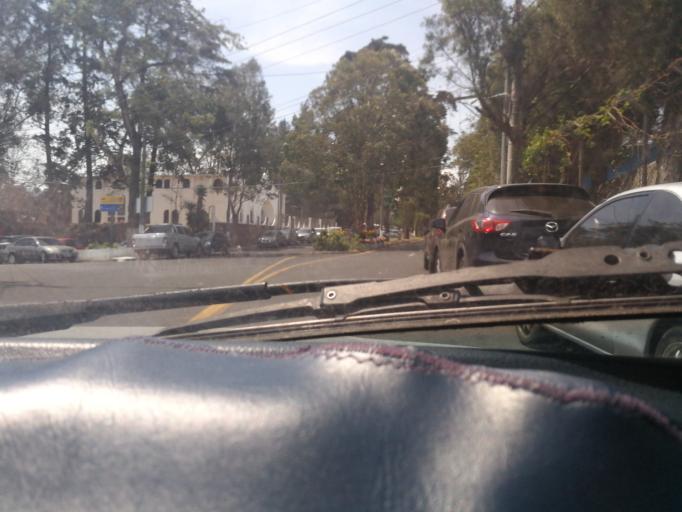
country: GT
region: Guatemala
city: Guatemala City
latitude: 14.6228
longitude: -90.4735
